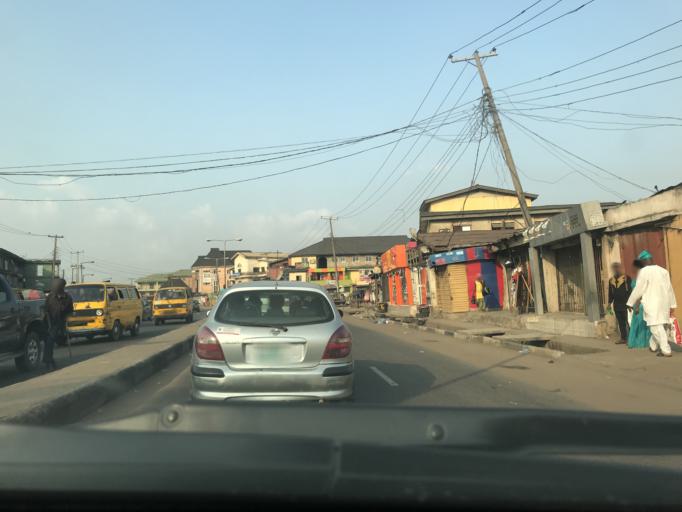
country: NG
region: Lagos
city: Agege
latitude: 6.5995
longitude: 3.2915
